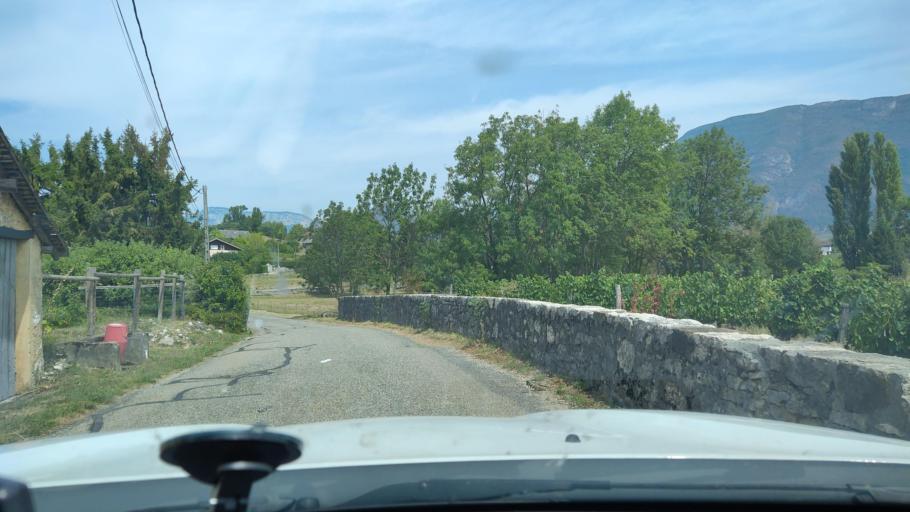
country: FR
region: Rhone-Alpes
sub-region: Departement de la Savoie
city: Les Marches
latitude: 45.5059
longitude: 5.9831
